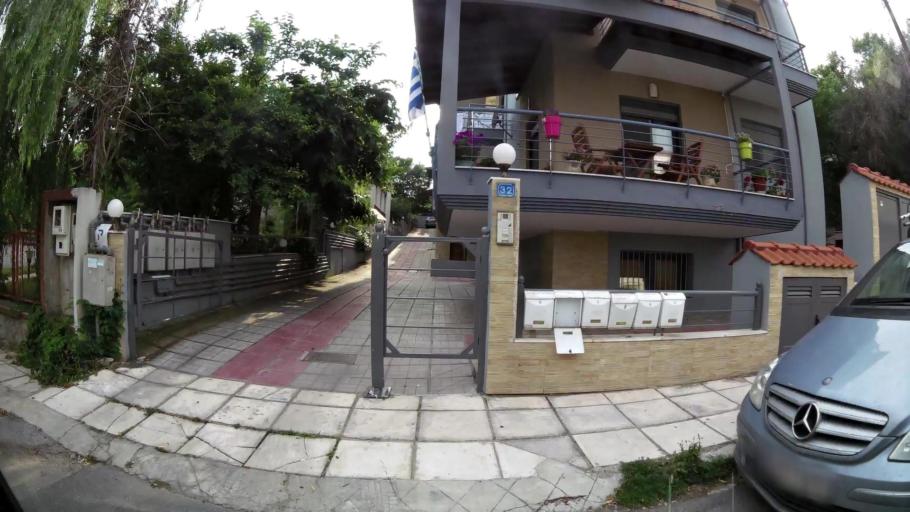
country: GR
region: Central Macedonia
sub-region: Nomos Thessalonikis
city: Oraiokastro
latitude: 40.7263
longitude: 22.9171
